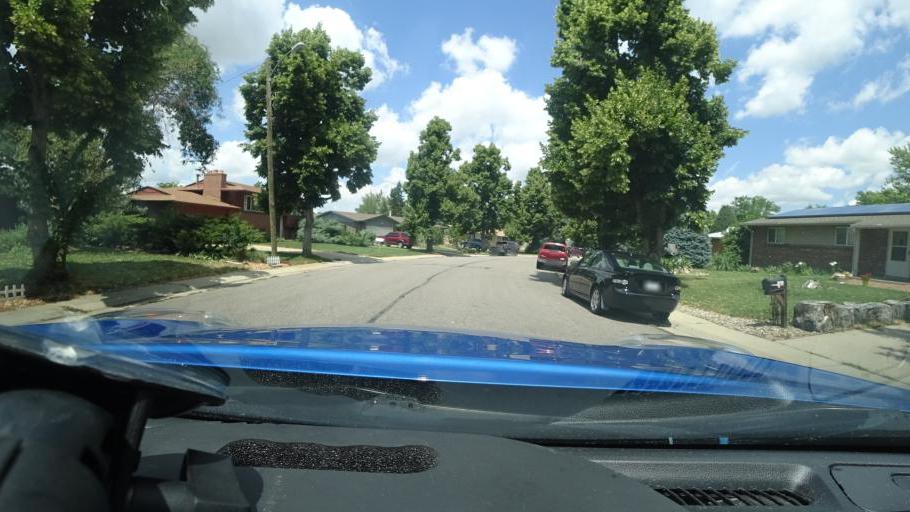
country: US
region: Colorado
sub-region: Adams County
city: Aurora
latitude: 39.7067
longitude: -104.8380
